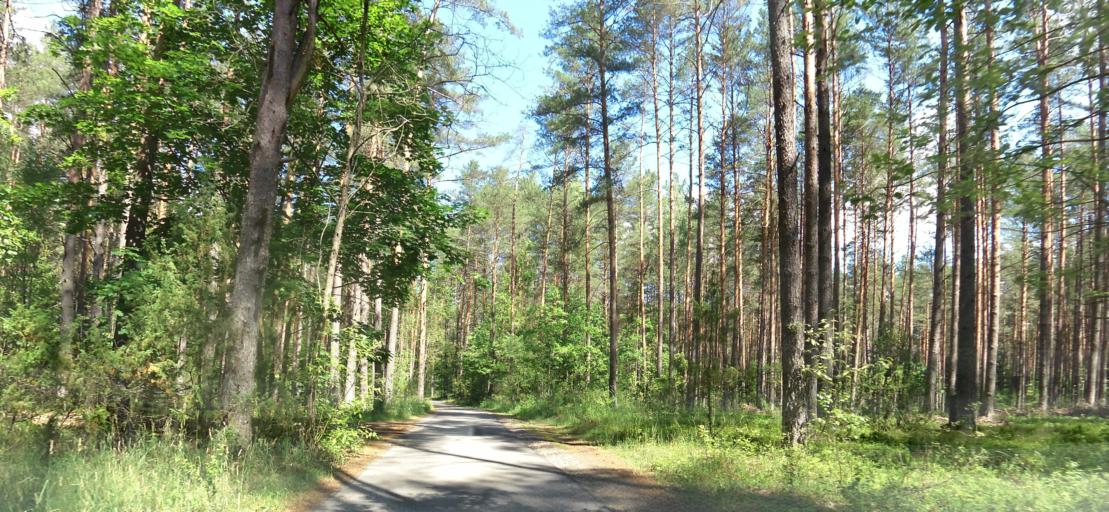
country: LT
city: Nemencine
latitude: 54.8088
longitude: 25.3946
